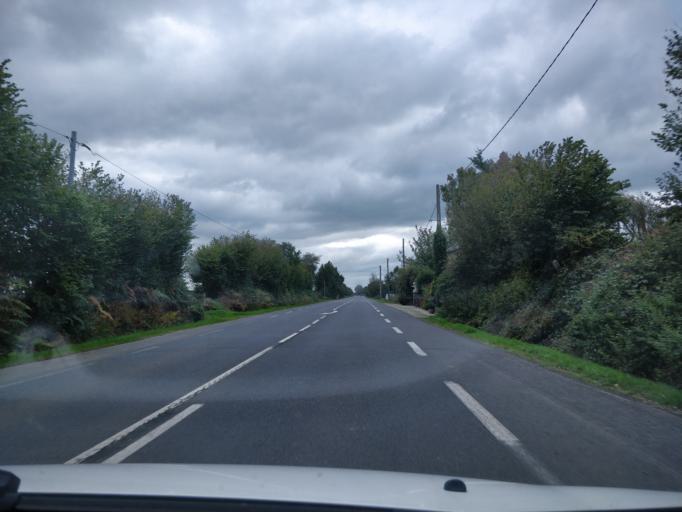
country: FR
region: Lower Normandy
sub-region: Departement du Calvados
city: Saint-Sever-Calvados
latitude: 48.8221
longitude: -1.1126
